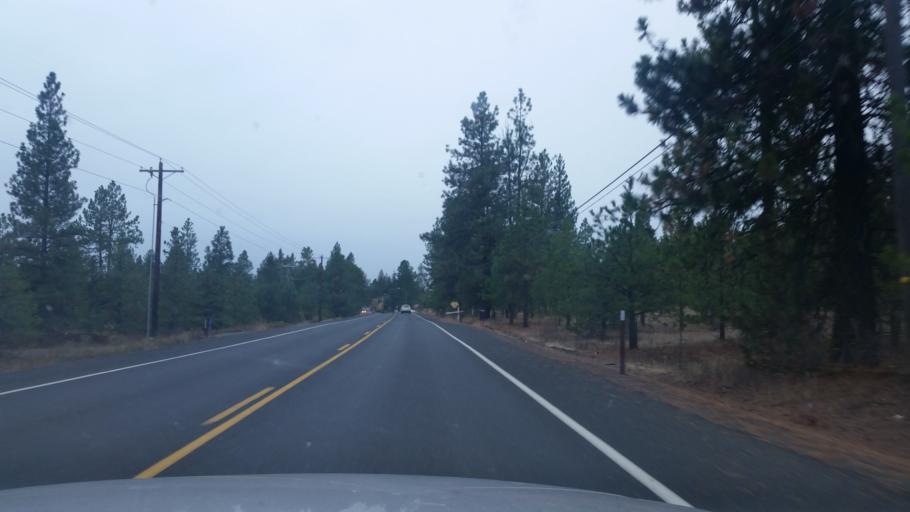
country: US
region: Washington
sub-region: Spokane County
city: Cheney
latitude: 47.5050
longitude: -117.5541
